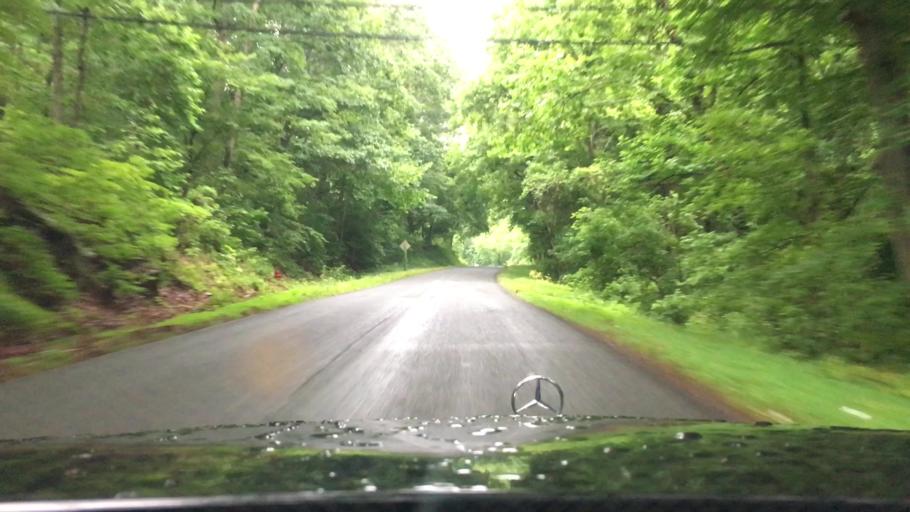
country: US
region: Virginia
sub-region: Pittsylvania County
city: Hurt
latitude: 37.0979
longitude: -79.3002
